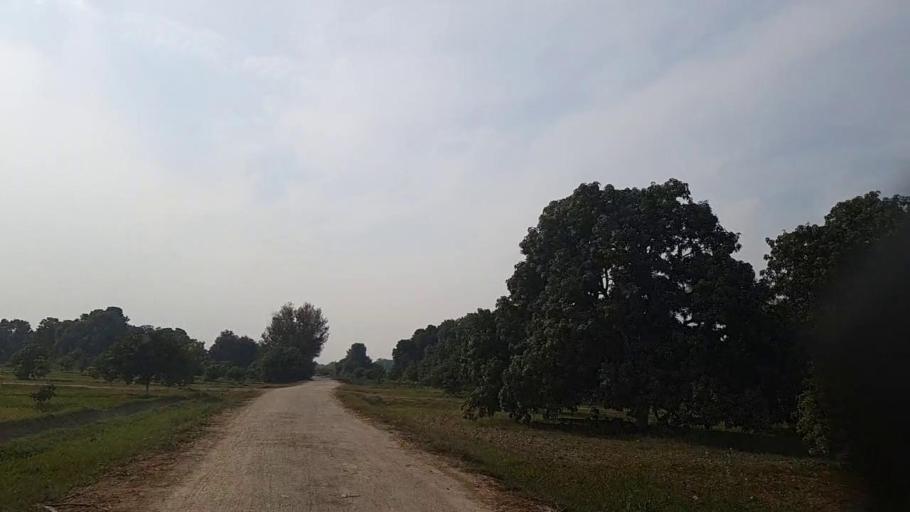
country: PK
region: Sindh
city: Daur
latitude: 26.3995
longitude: 68.2053
